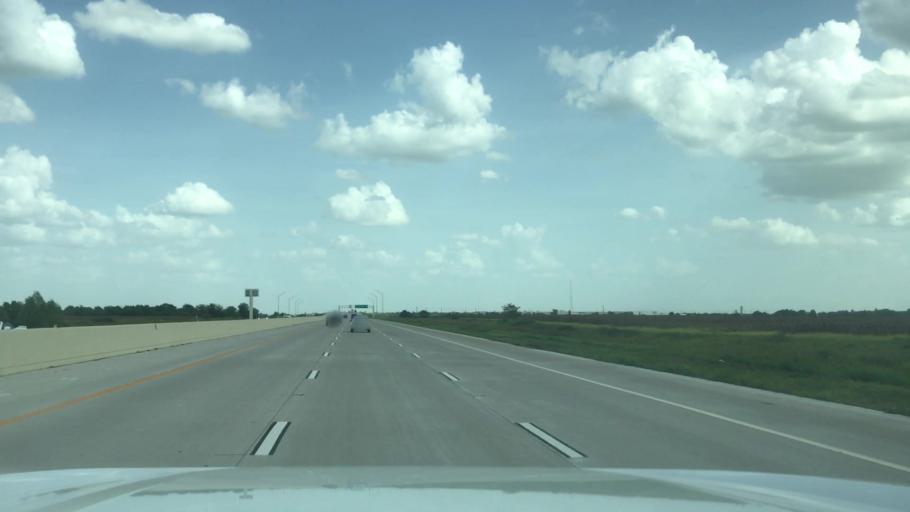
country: US
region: Texas
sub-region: Waller County
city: Waller
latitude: 30.0537
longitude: -95.8833
